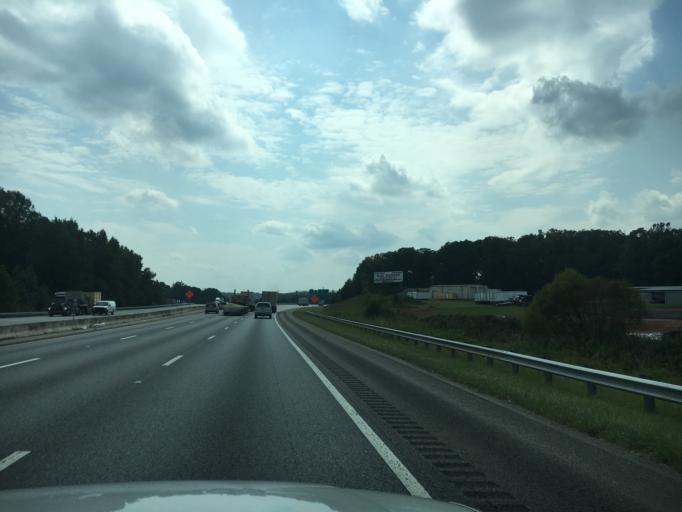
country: US
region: South Carolina
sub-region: Anderson County
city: Piedmont
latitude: 34.6985
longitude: -82.5028
